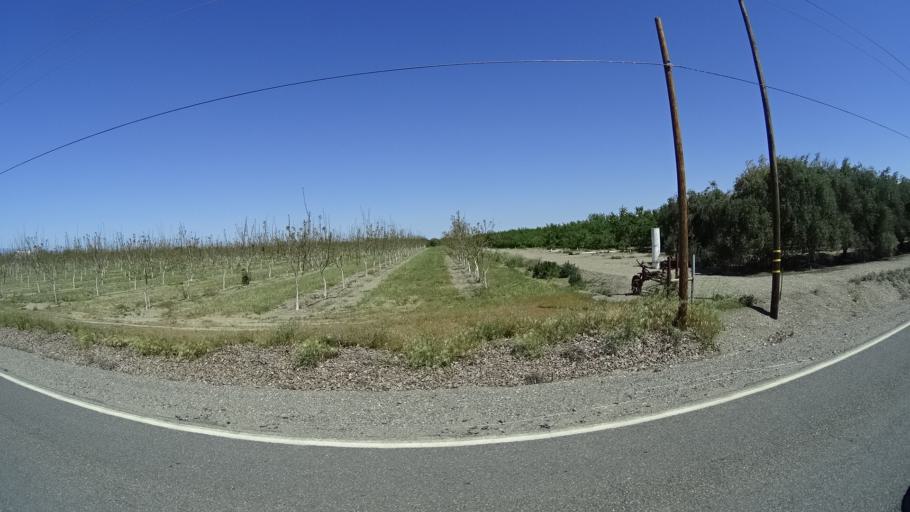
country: US
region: California
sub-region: Glenn County
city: Orland
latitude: 39.7106
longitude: -122.1377
